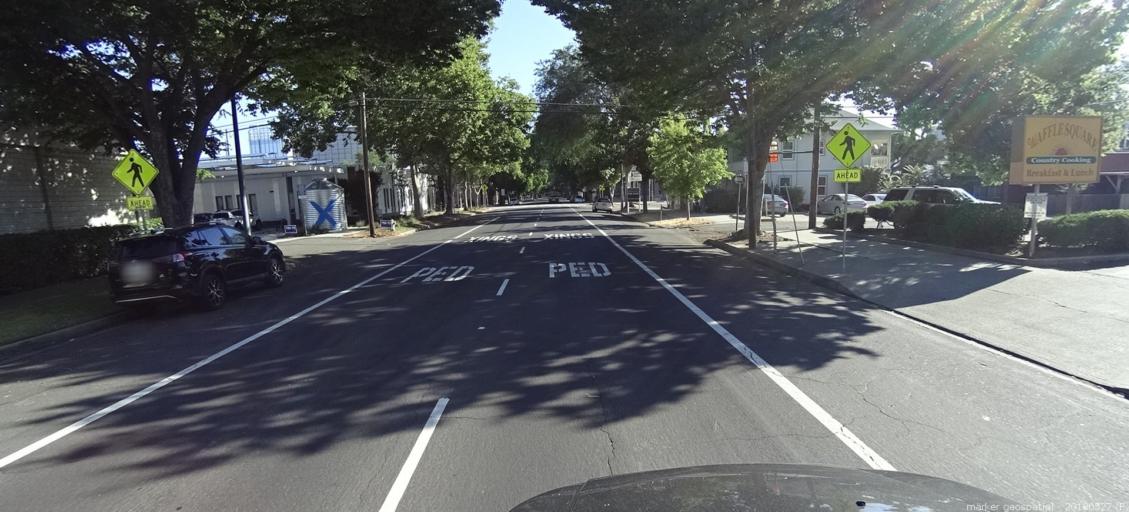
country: US
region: California
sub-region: Sacramento County
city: Sacramento
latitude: 38.5707
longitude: -121.4977
